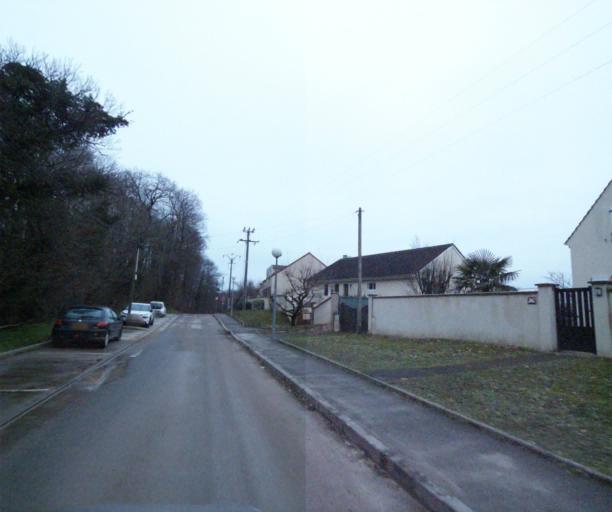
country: FR
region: Ile-de-France
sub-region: Departement de Seine-et-Marne
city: Longperrier
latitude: 49.0591
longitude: 2.6665
